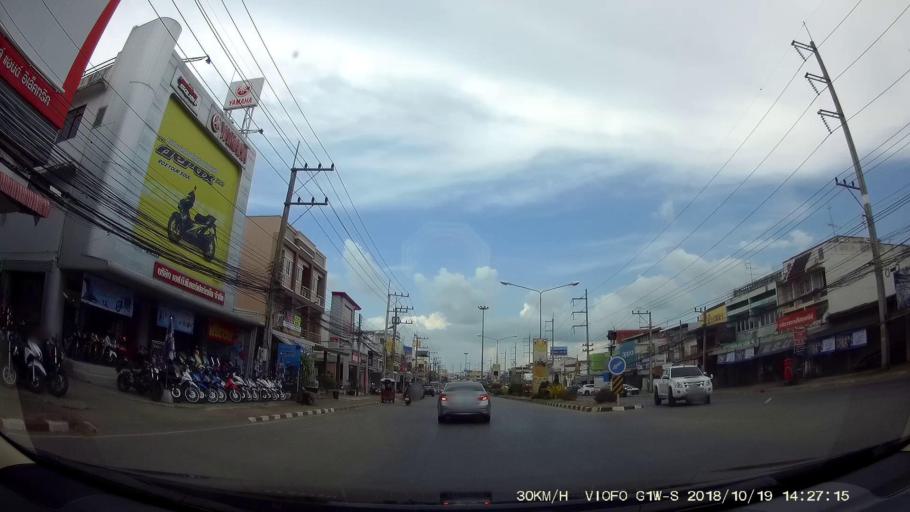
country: TH
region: Chaiyaphum
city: Kaeng Khro
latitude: 16.1107
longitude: 102.2582
